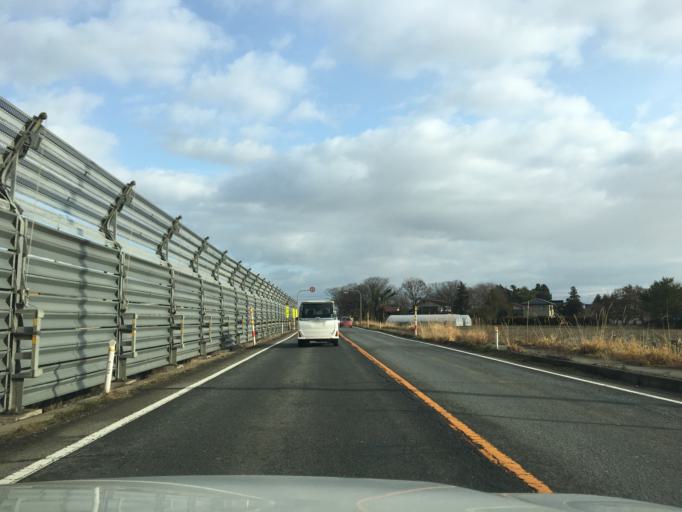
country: JP
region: Yamagata
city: Sakata
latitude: 38.8422
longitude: 139.8488
